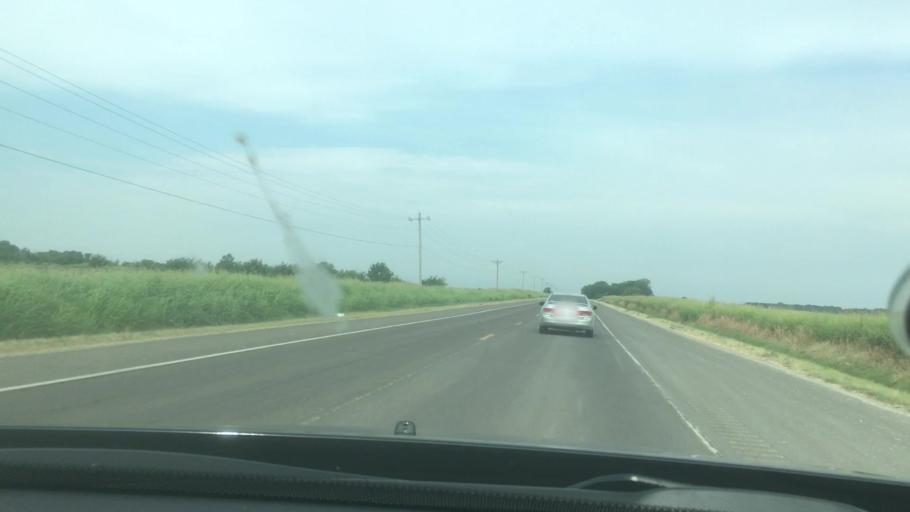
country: US
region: Oklahoma
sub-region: Garvin County
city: Maysville
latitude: 34.8192
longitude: -97.4578
